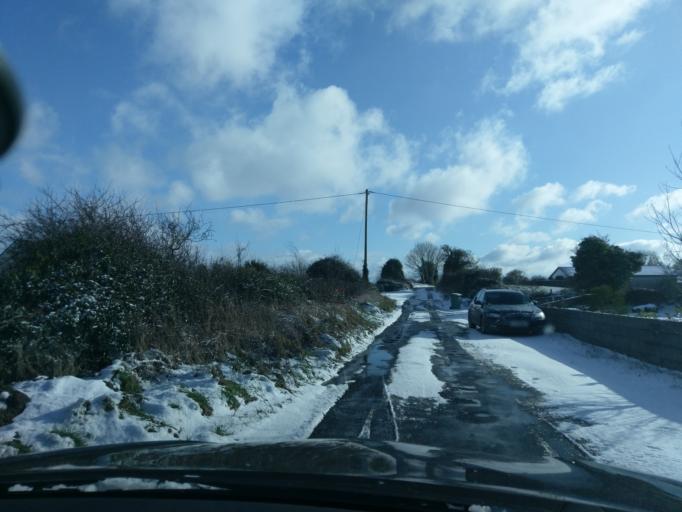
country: IE
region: Connaught
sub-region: County Galway
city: Athenry
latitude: 53.1936
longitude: -8.7505
